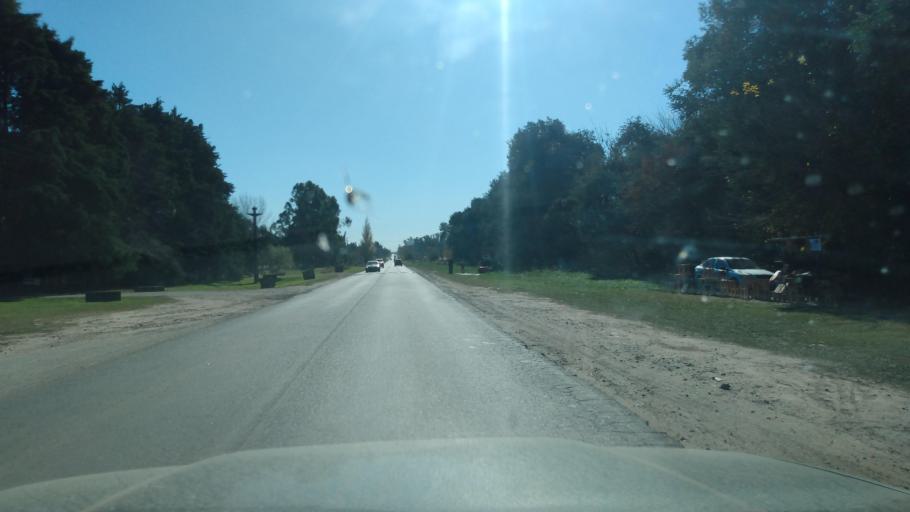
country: AR
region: Buenos Aires
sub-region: Partido de Lujan
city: Lujan
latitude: -34.5294
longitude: -59.1687
